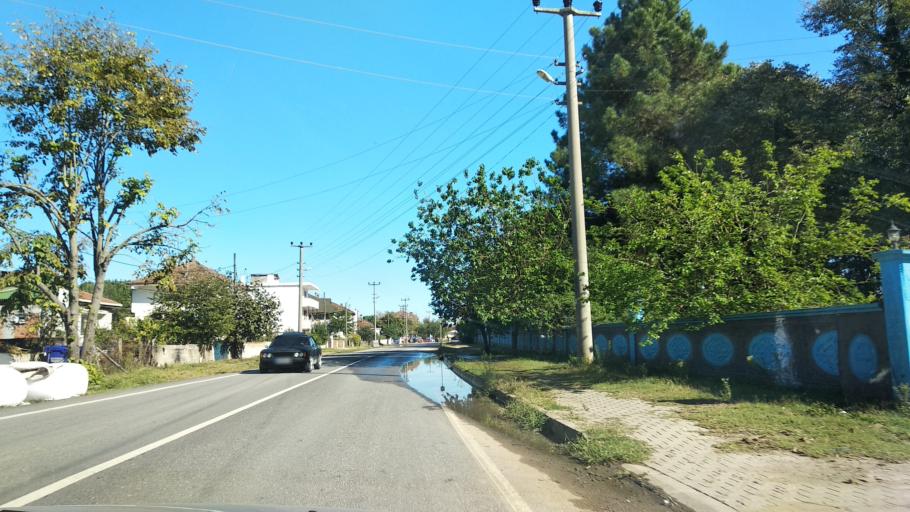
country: TR
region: Sakarya
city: Karasu
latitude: 41.1182
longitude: 30.6299
